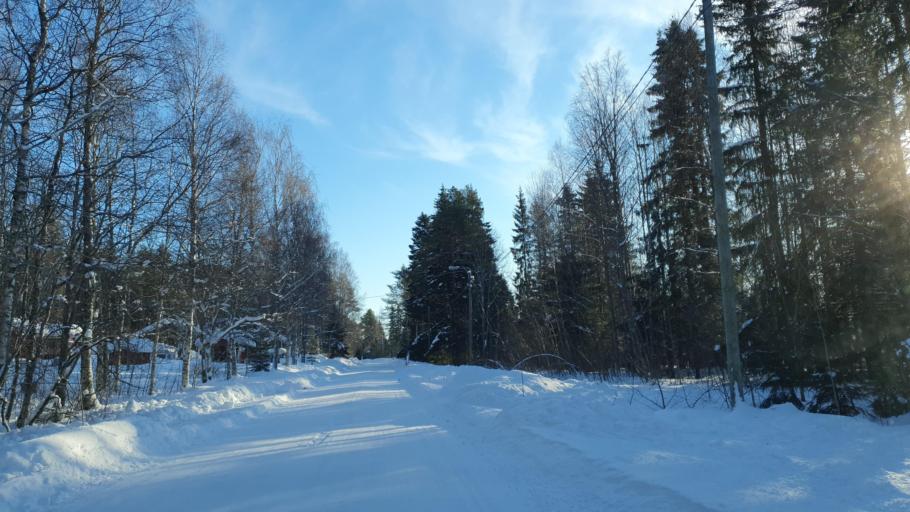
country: FI
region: Northern Ostrobothnia
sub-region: Oulu
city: Haukipudas
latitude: 65.1925
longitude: 25.4198
